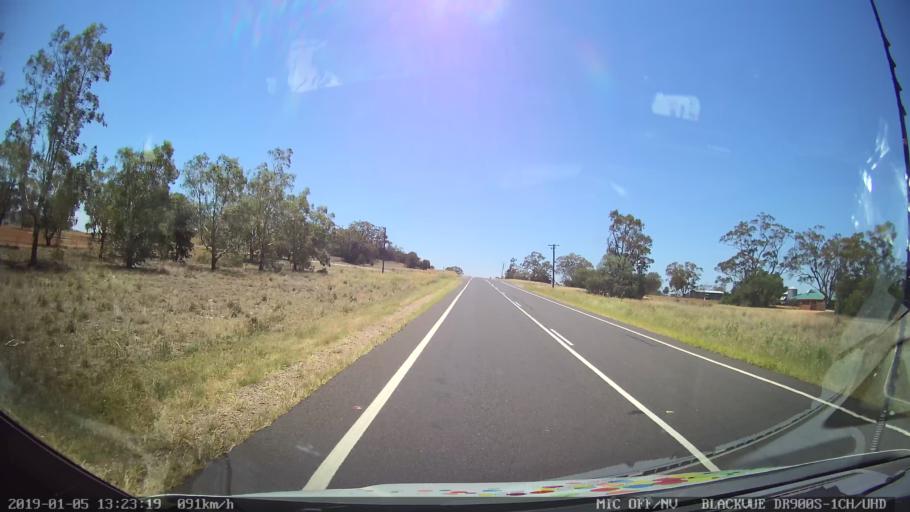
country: AU
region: New South Wales
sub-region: Gunnedah
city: Gunnedah
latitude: -31.0789
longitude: 149.9737
